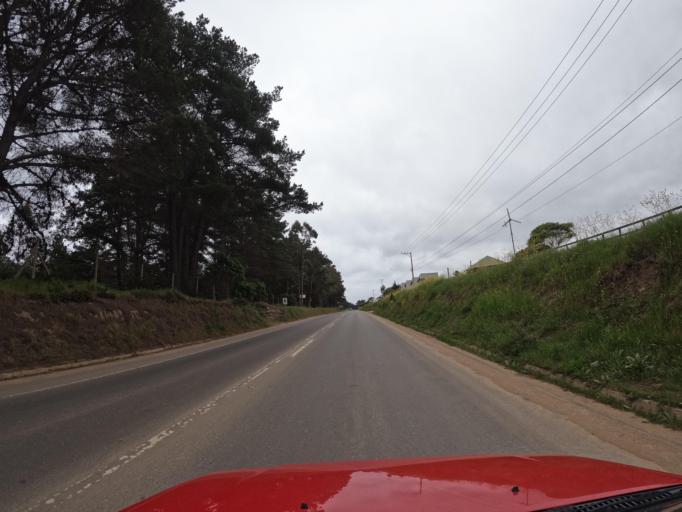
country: CL
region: O'Higgins
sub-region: Provincia de Colchagua
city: Santa Cruz
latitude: -34.4250
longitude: -72.0310
